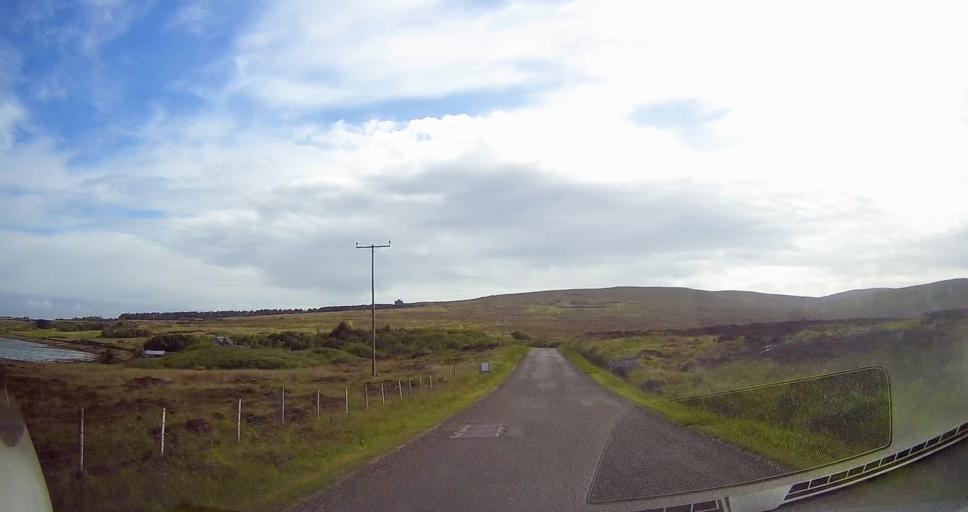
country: GB
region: Scotland
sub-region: Orkney Islands
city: Stromness
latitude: 58.8420
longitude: -3.2133
